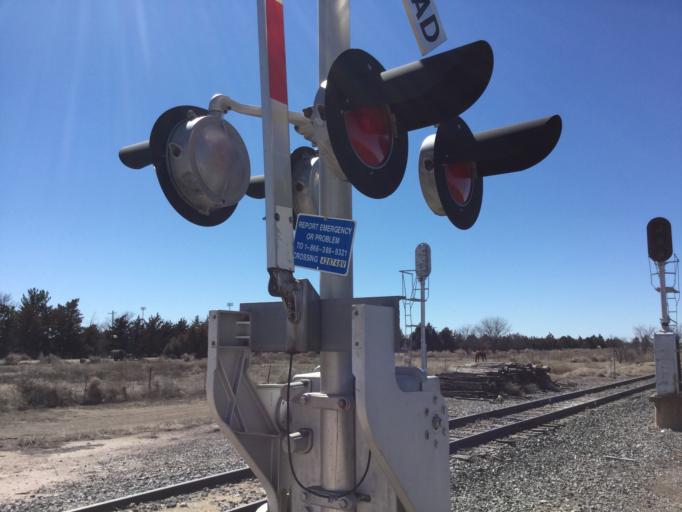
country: US
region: Kansas
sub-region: Wichita County
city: Leoti
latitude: 38.4856
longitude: -101.3676
